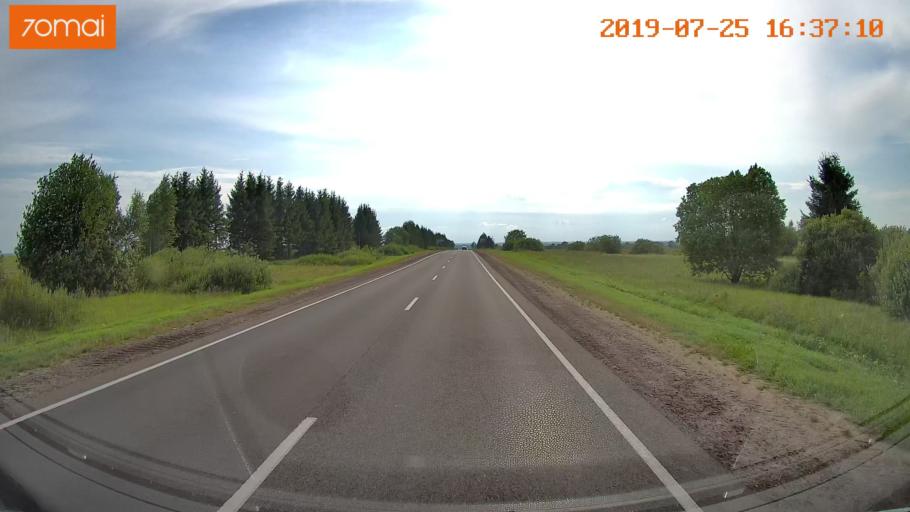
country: RU
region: Ivanovo
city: Privolzhsk
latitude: 57.3918
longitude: 41.3831
